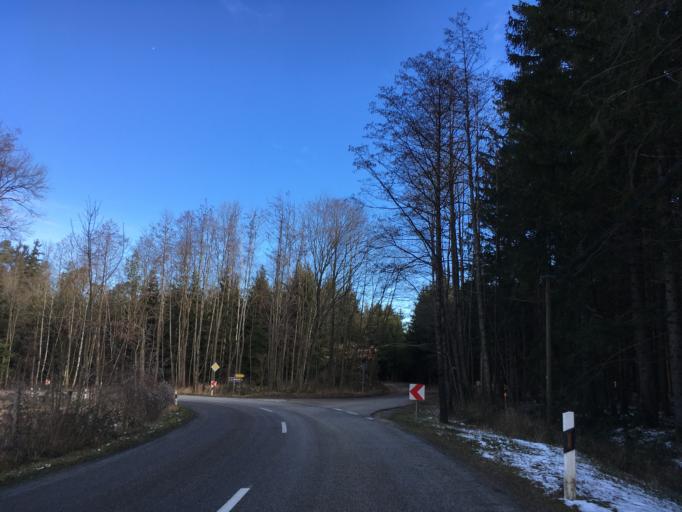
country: DE
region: Bavaria
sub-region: Upper Bavaria
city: Reichertsheim
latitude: 48.2195
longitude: 12.2756
